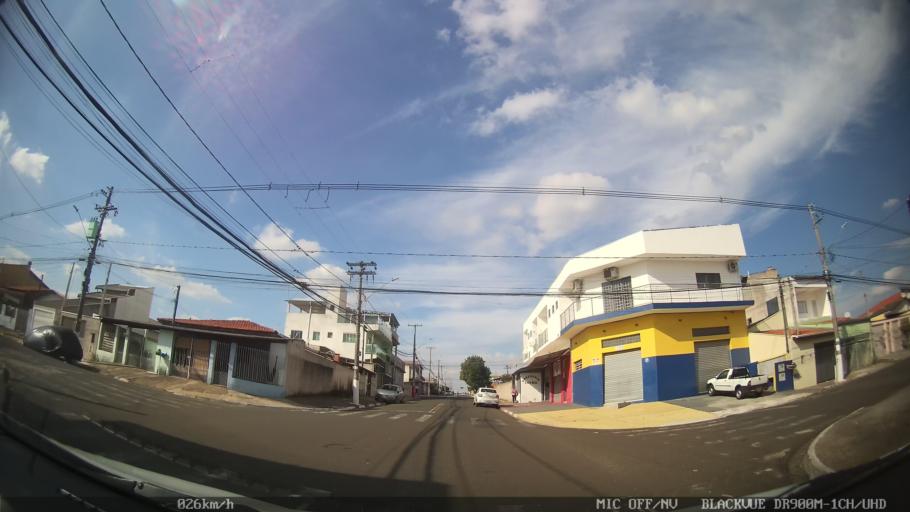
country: BR
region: Sao Paulo
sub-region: Hortolandia
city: Hortolandia
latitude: -22.8967
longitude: -47.2326
